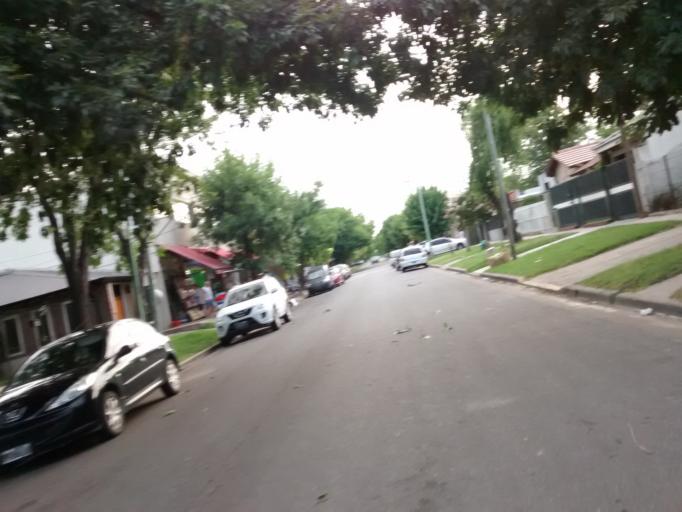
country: AR
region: Buenos Aires
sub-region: Partido de La Plata
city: La Plata
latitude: -34.8657
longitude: -58.0534
